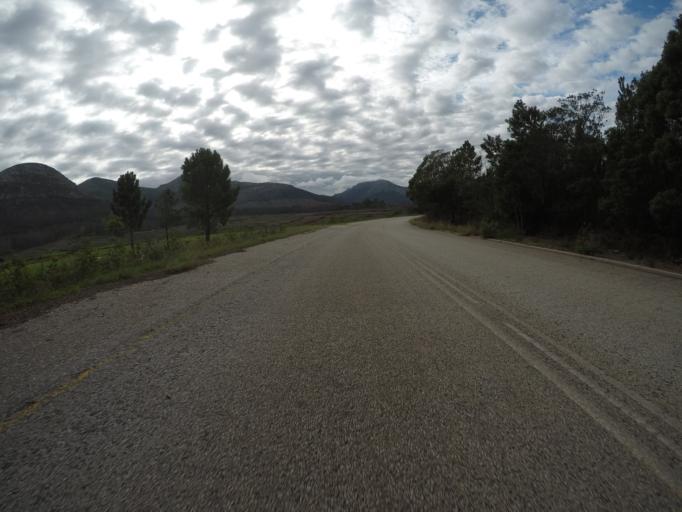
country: ZA
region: Eastern Cape
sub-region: Cacadu District Municipality
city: Kareedouw
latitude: -34.0118
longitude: 24.3100
